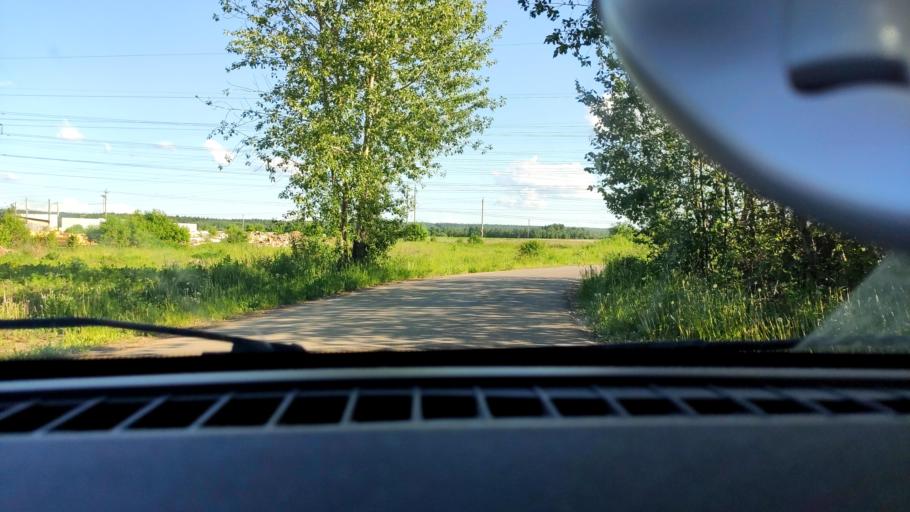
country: RU
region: Perm
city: Ferma
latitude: 57.9169
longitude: 56.3389
